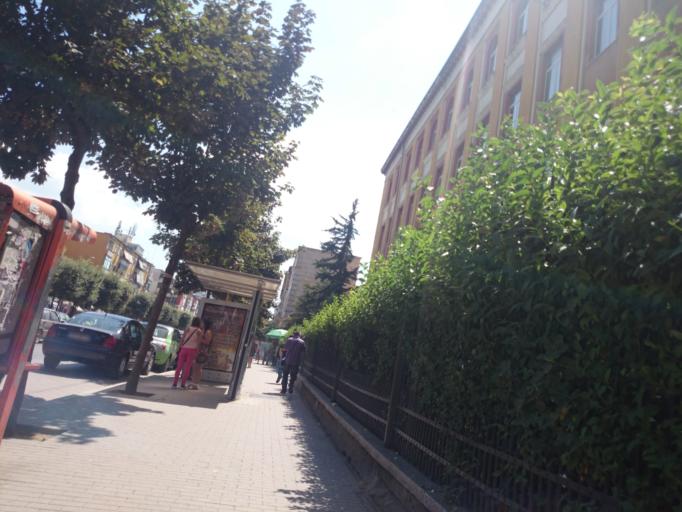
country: AL
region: Tirane
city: Tirana
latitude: 41.3347
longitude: 19.8165
